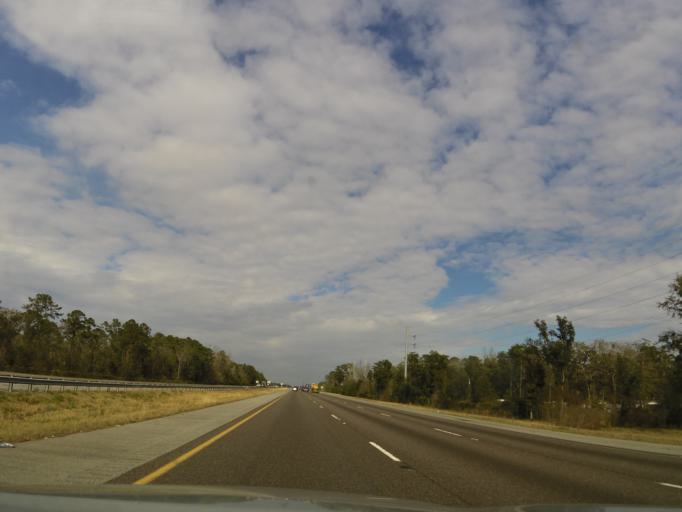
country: US
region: Georgia
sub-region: Liberty County
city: Midway
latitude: 31.8156
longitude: -81.3624
